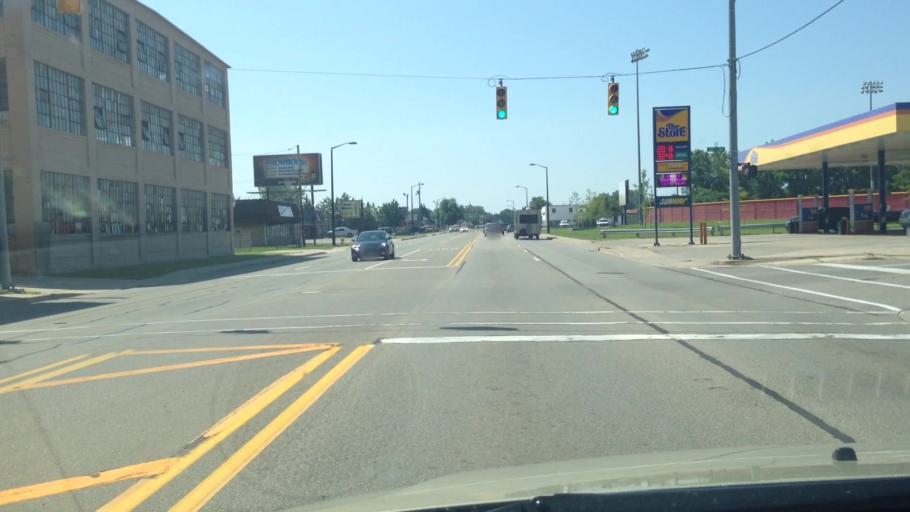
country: US
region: Michigan
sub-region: Menominee County
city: Menominee
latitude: 45.1262
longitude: -87.6130
